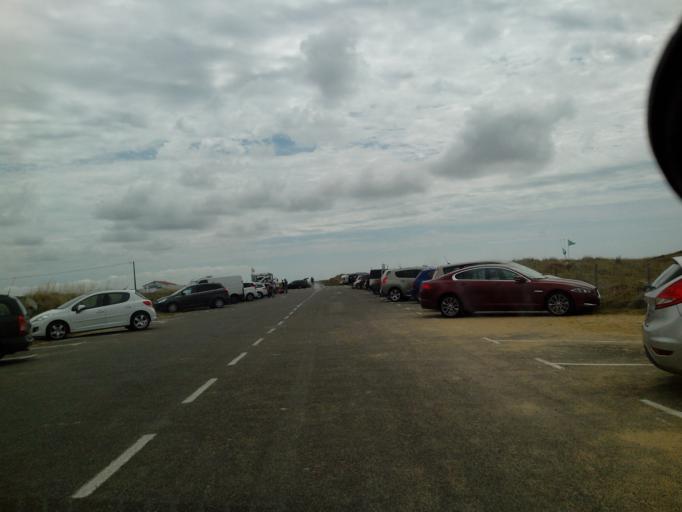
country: FR
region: Brittany
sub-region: Departement du Morbihan
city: Erdeven
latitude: 47.6132
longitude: -3.1692
